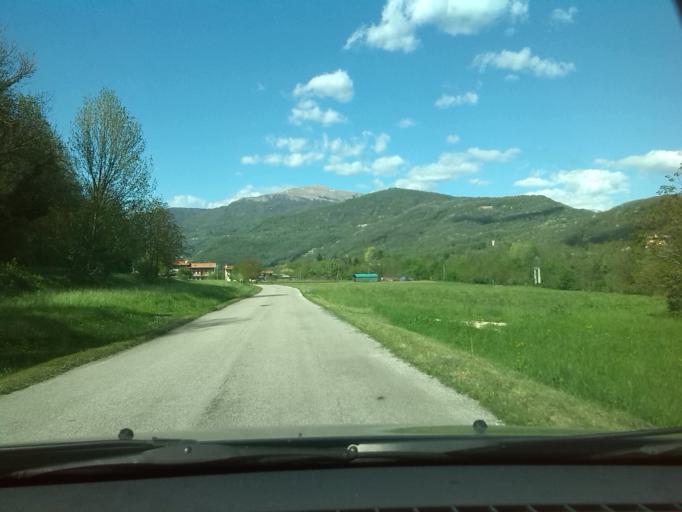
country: IT
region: Friuli Venezia Giulia
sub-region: Provincia di Udine
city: San Pietro al Natisone
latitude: 46.1285
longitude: 13.4812
